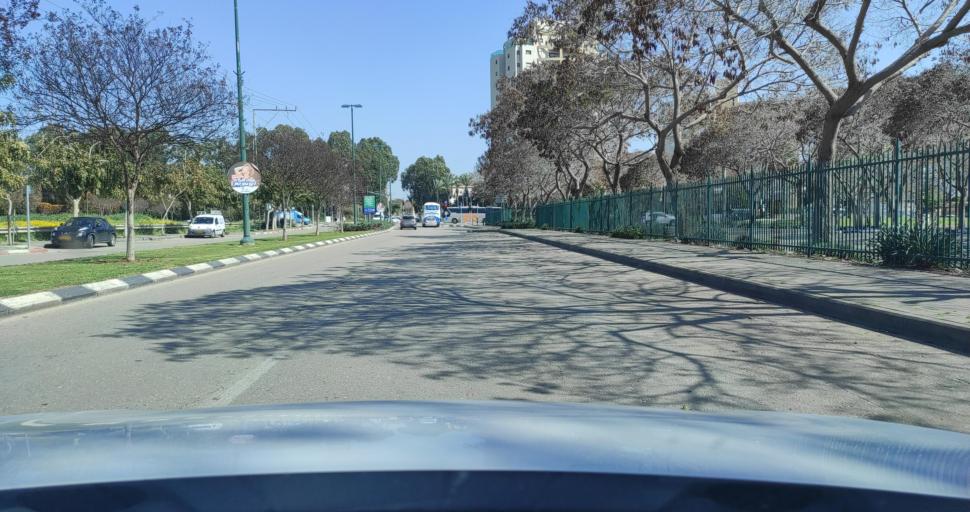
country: IL
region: Central District
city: Bet Yizhaq
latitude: 32.3114
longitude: 34.8746
